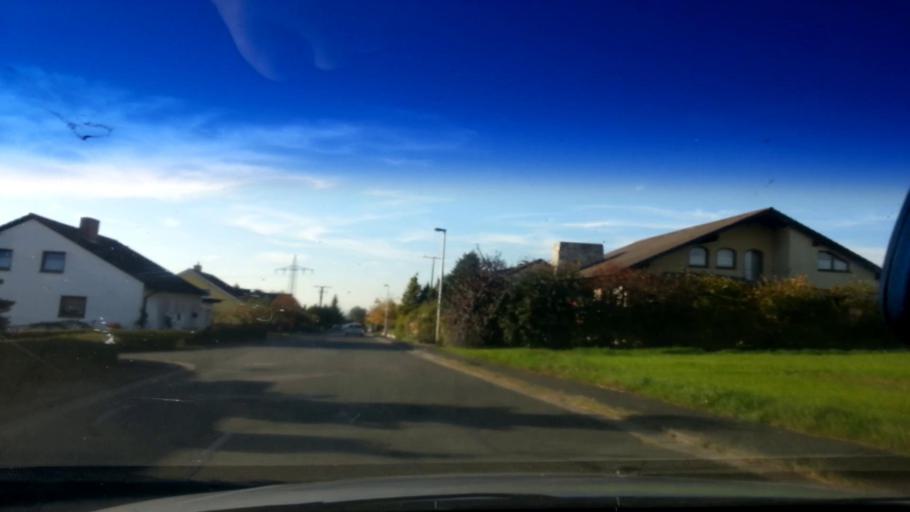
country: DE
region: Bavaria
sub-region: Upper Franconia
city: Litzendorf
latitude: 49.9125
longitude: 10.9982
